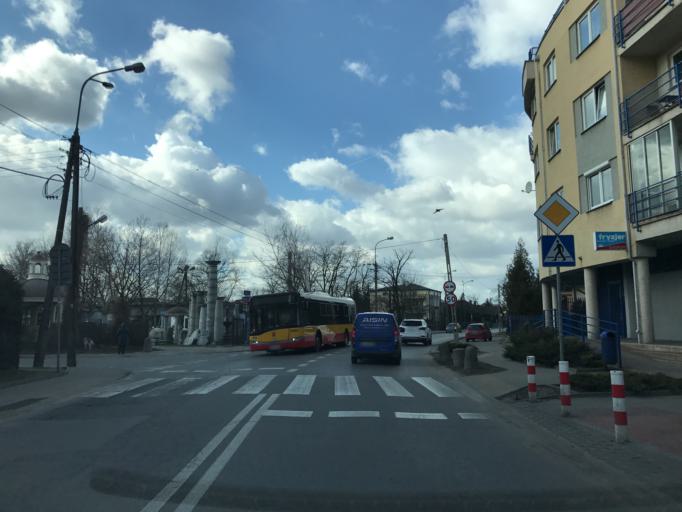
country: PL
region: Masovian Voivodeship
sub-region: Warszawa
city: Rembertow
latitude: 52.2602
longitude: 21.1610
